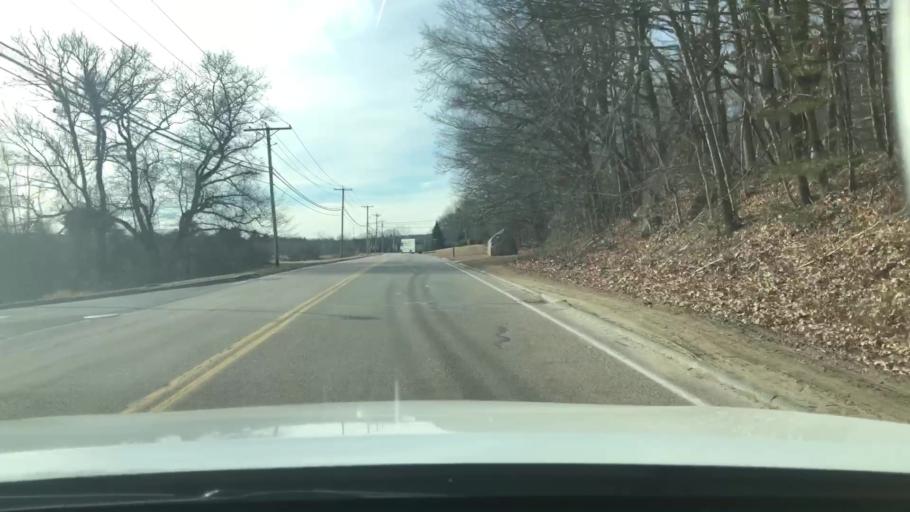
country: US
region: Massachusetts
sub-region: Worcester County
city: Grafton
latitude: 42.2000
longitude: -71.7087
